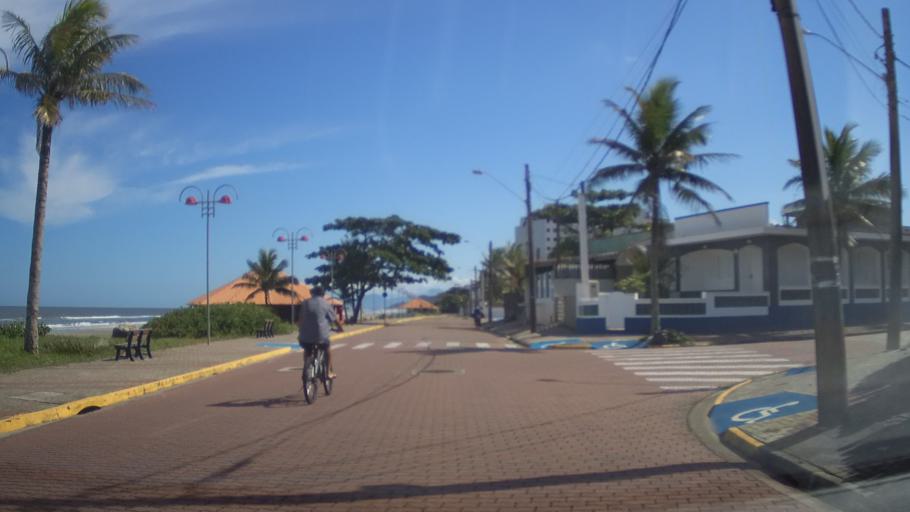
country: BR
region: Sao Paulo
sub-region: Itanhaem
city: Itanhaem
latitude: -24.1746
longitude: -46.7658
